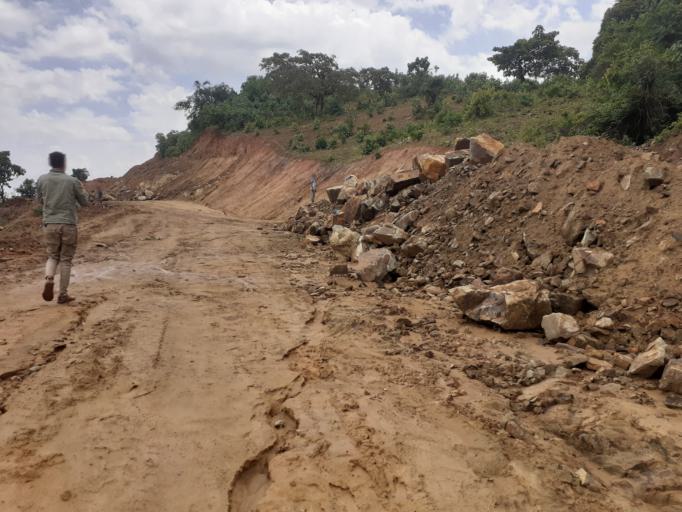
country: ET
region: Oromiya
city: Gimbi
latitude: 9.3242
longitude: 35.6922
